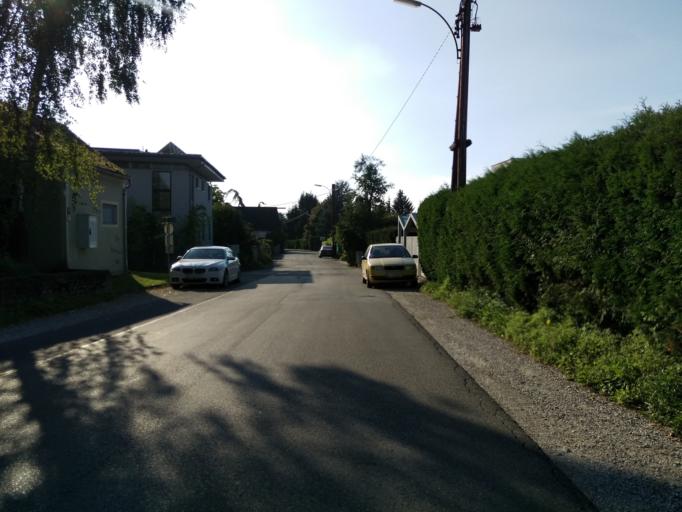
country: AT
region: Styria
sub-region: Graz Stadt
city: Mariatrost
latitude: 47.0732
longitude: 15.4878
